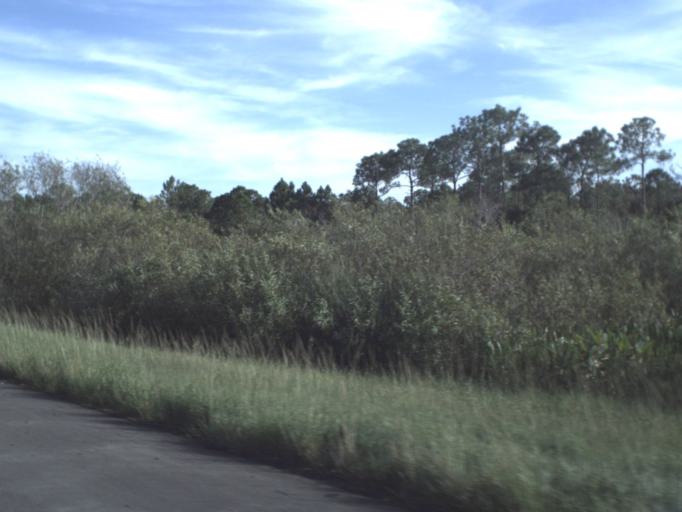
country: US
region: Florida
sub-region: Lee County
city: Suncoast Estates
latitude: 26.8044
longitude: -81.9243
